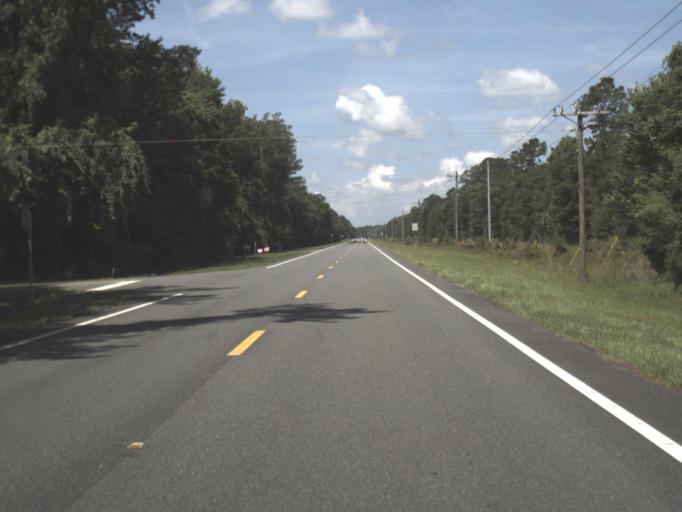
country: US
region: Florida
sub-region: Levy County
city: Chiefland
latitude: 29.3222
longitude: -82.7781
